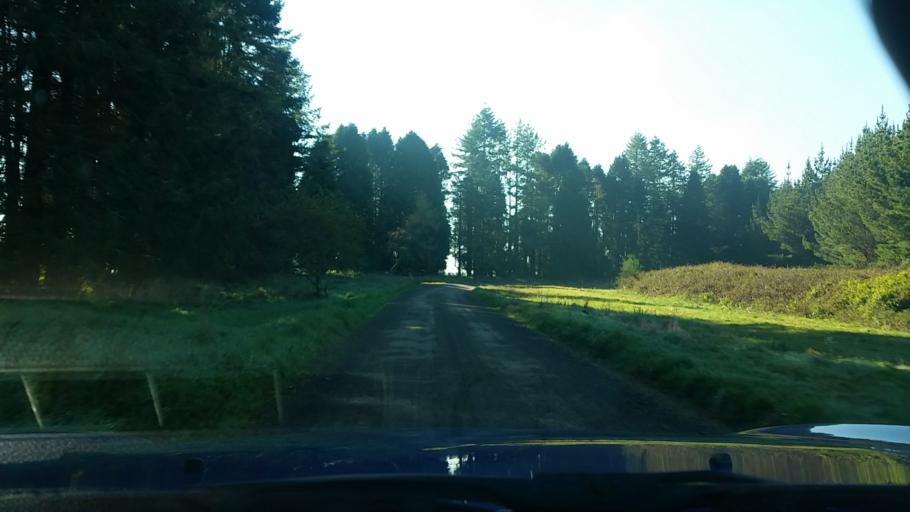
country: NZ
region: Bay of Plenty
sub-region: Whakatane District
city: Murupara
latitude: -38.3483
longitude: 176.5232
